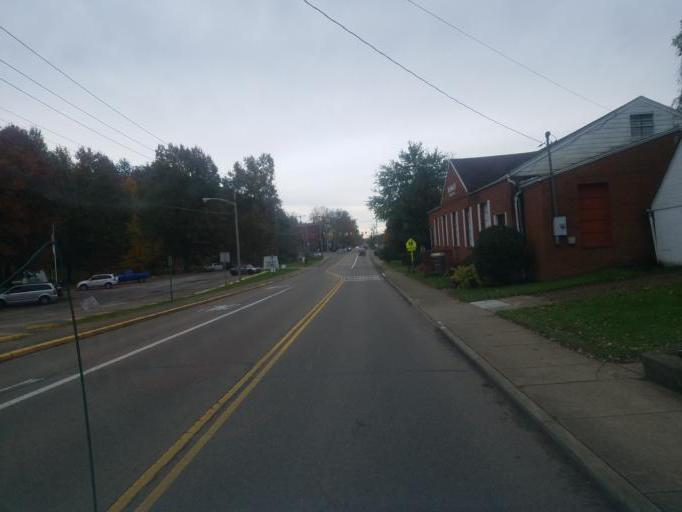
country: US
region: Ohio
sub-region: Washington County
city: Marietta
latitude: 39.4206
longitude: -81.4495
